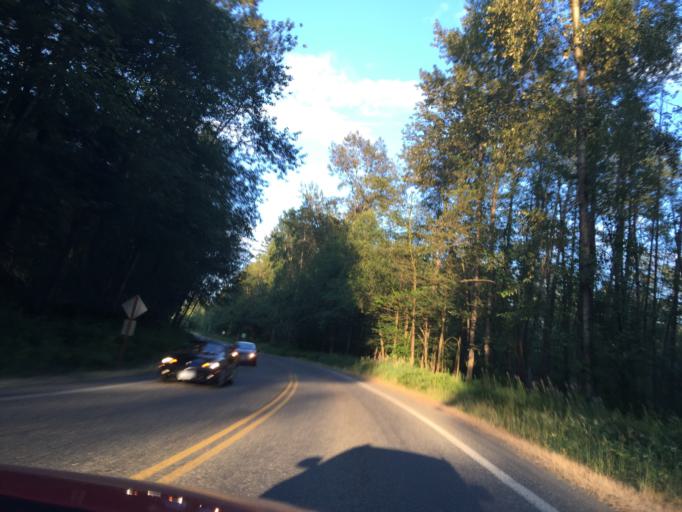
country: US
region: Washington
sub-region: Whatcom County
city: Birch Bay
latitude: 48.9356
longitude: -122.6580
